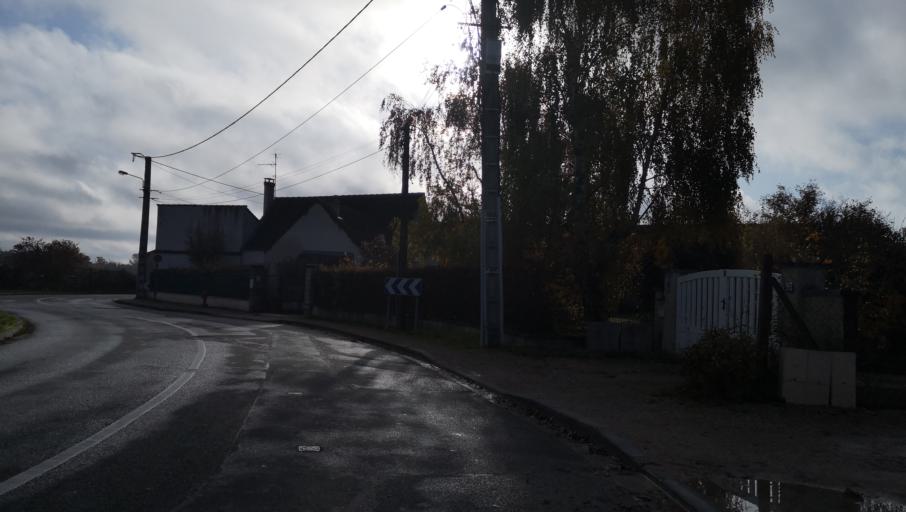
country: FR
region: Centre
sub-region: Departement du Loiret
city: Semoy
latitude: 47.9151
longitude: 1.9389
